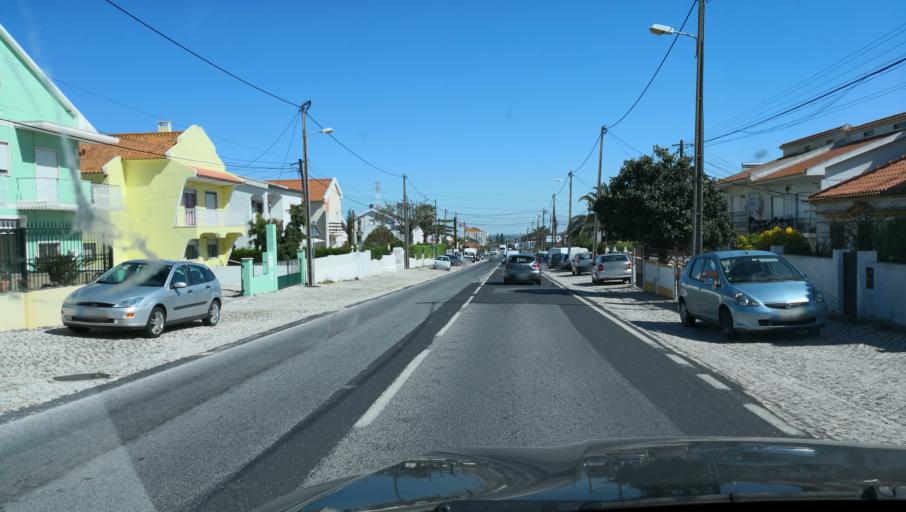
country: PT
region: Setubal
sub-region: Palmela
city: Palmela
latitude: 38.5794
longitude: -8.8902
